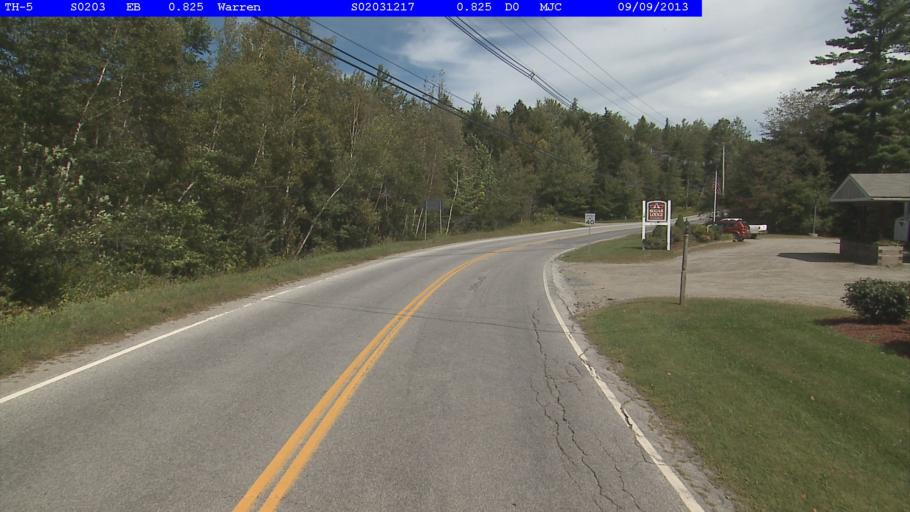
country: US
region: Vermont
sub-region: Addison County
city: Bristol
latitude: 44.1426
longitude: -72.8840
